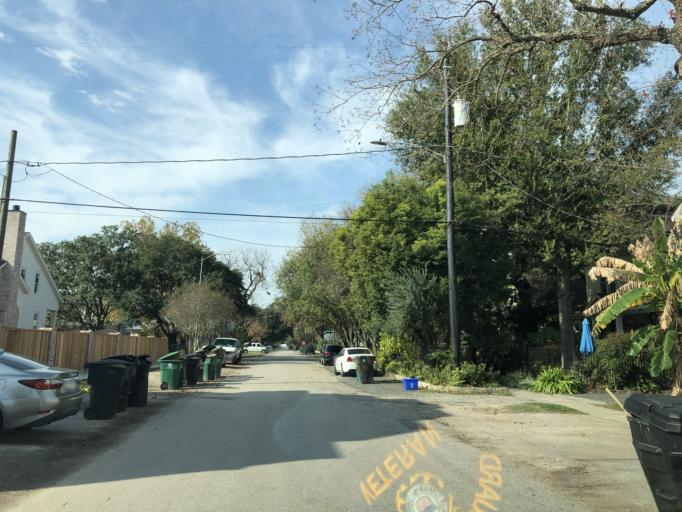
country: US
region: Texas
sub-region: Harris County
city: Houston
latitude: 29.7943
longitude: -95.3945
